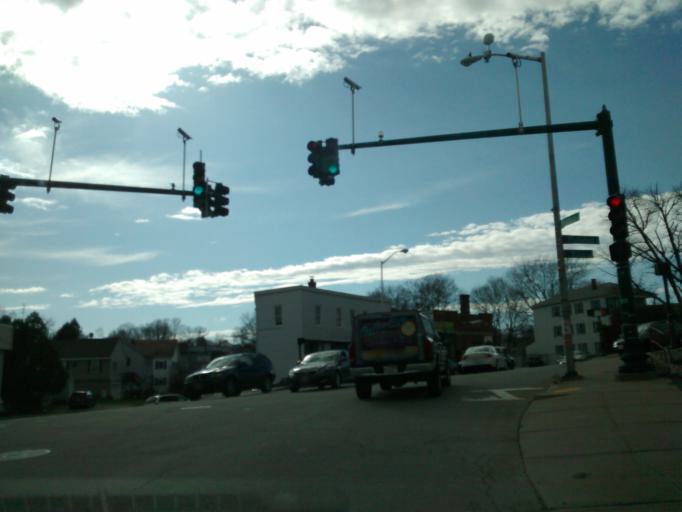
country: US
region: Massachusetts
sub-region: Worcester County
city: Sunderland
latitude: 42.2509
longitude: -71.7808
